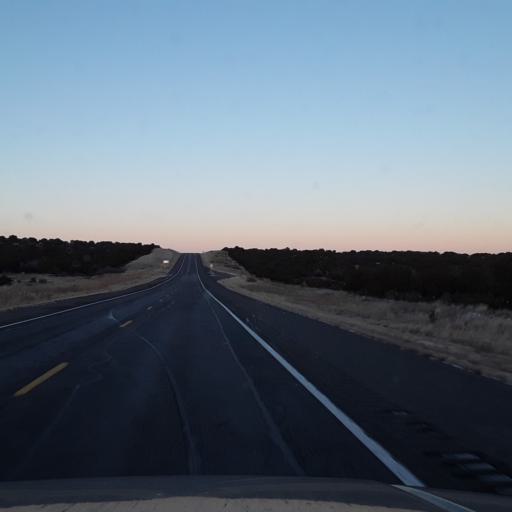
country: US
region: New Mexico
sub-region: Guadalupe County
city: Santa Rosa
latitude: 34.5277
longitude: -105.3241
